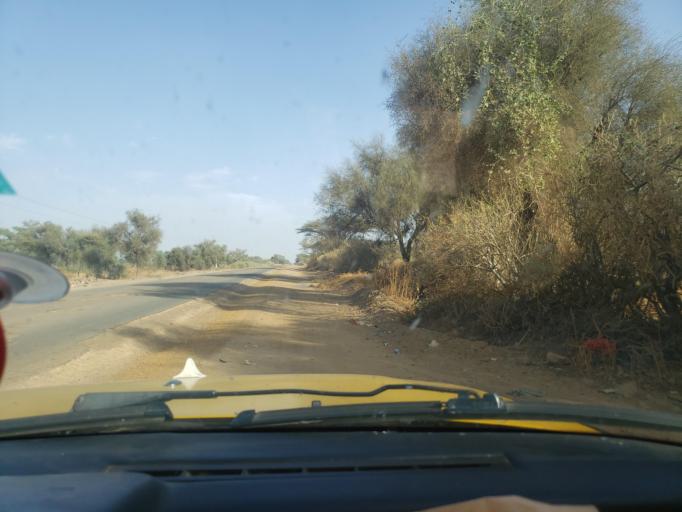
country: SN
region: Louga
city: Louga
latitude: 15.5094
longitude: -15.9789
